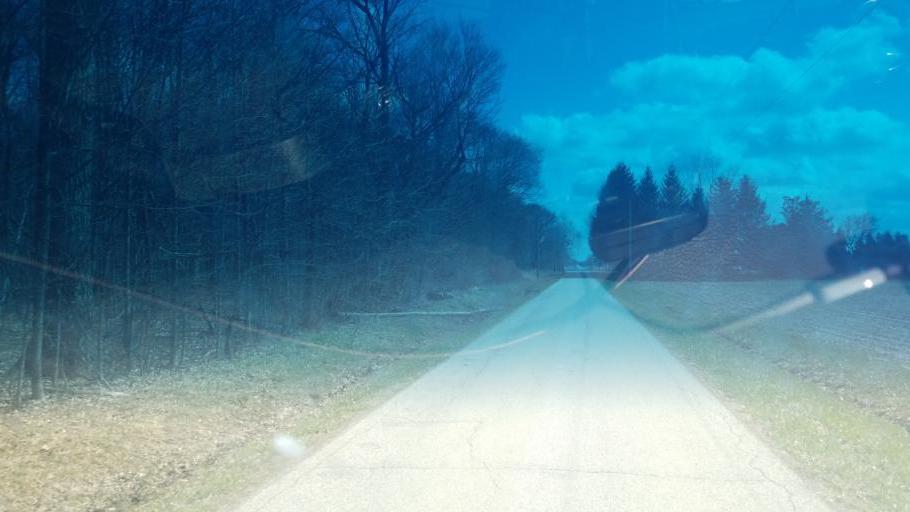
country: US
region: Ohio
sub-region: Crawford County
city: Bucyrus
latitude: 40.8485
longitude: -83.0628
